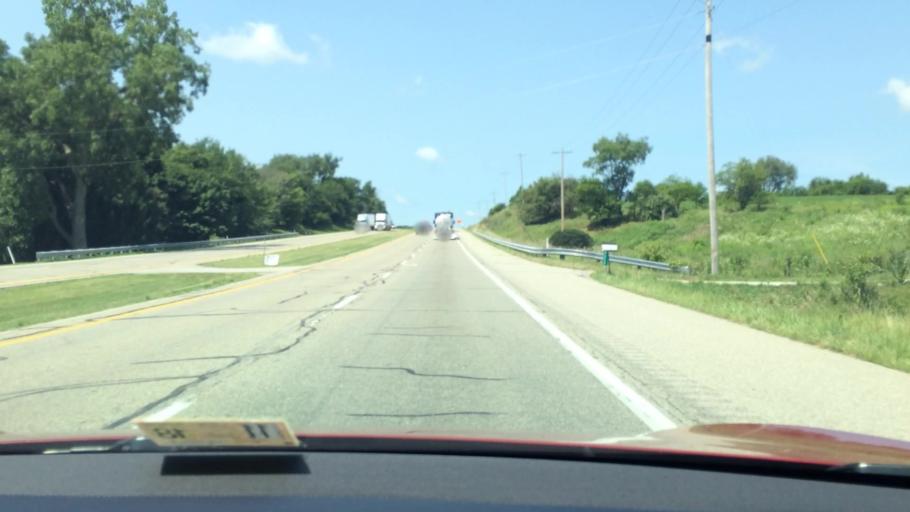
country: US
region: Indiana
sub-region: LaPorte County
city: Hudson Lake
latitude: 41.6727
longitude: -86.5523
